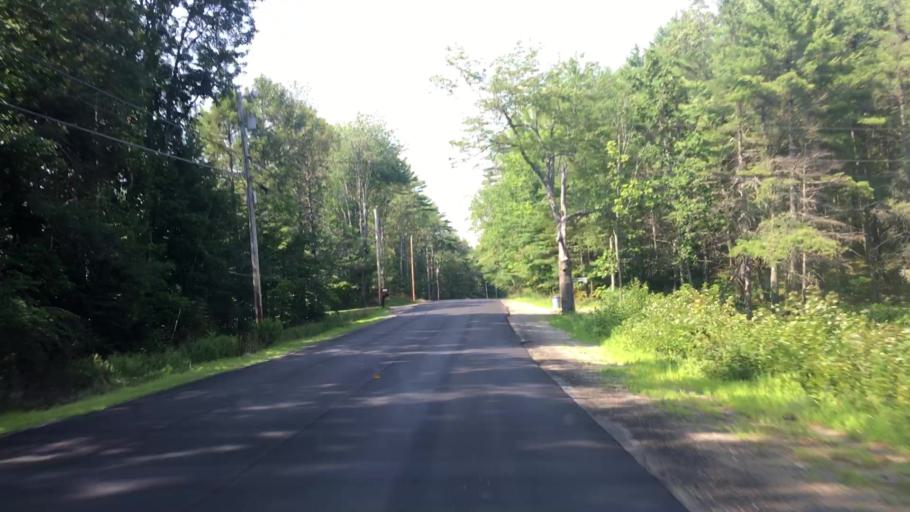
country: US
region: Maine
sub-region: Sagadahoc County
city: North Bath
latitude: 43.9381
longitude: -69.7999
